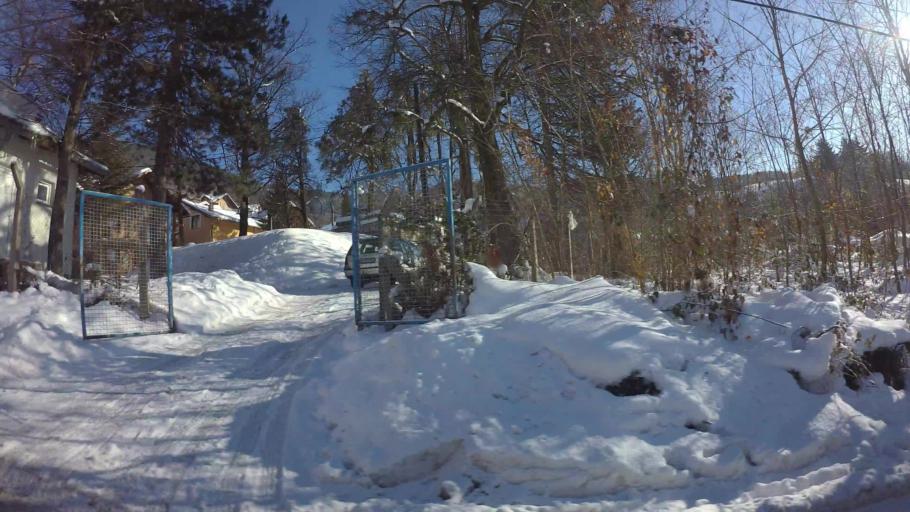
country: BA
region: Federation of Bosnia and Herzegovina
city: Kobilja Glava
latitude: 43.8920
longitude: 18.4172
